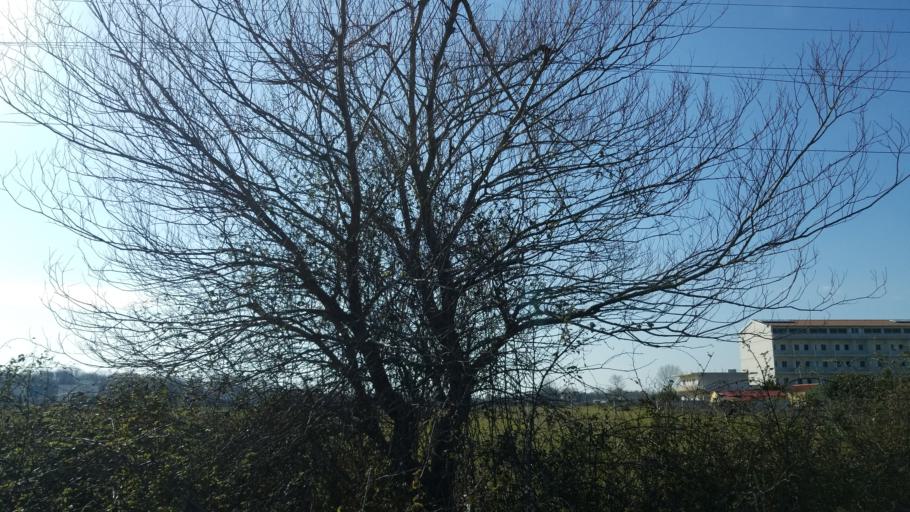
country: AL
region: Shkoder
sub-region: Rrethi i Shkodres
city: Velipoje
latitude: 41.8691
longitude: 19.4115
